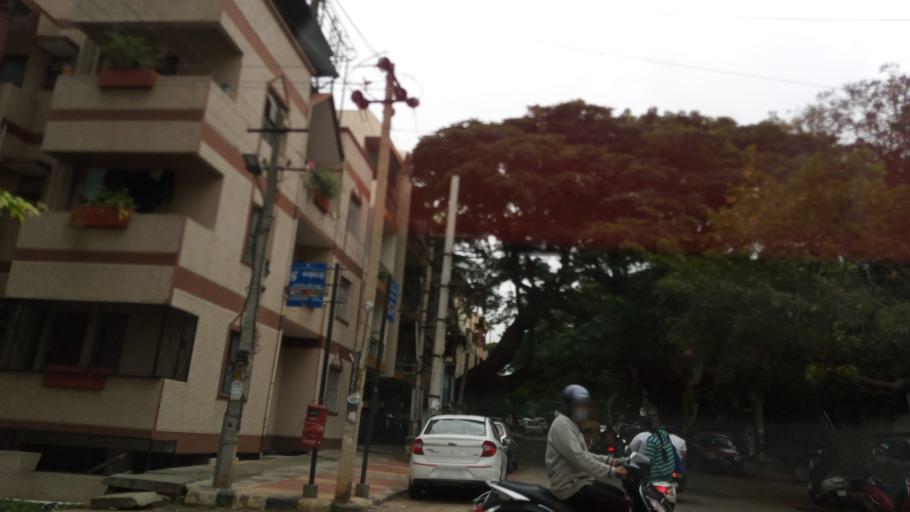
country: IN
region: Karnataka
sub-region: Bangalore Urban
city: Bangalore
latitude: 12.9375
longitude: 77.5410
